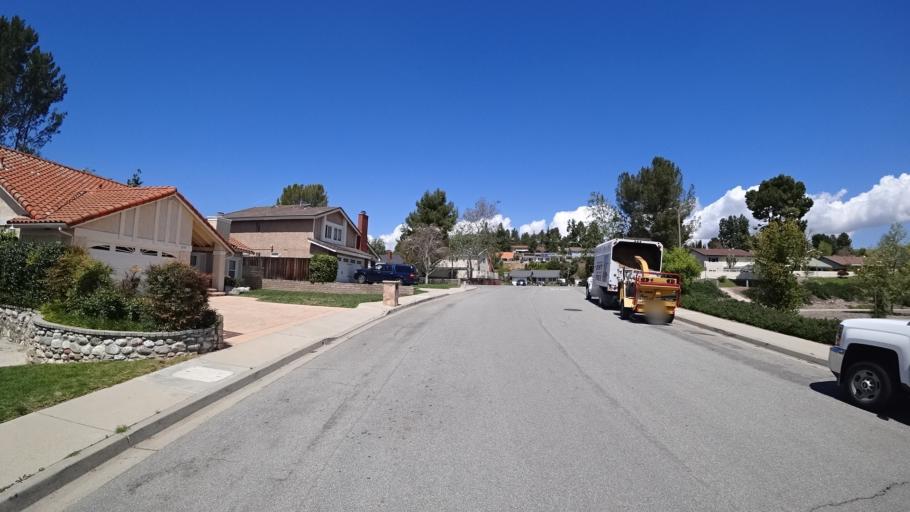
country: US
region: California
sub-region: Ventura County
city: Thousand Oaks
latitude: 34.2167
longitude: -118.8460
